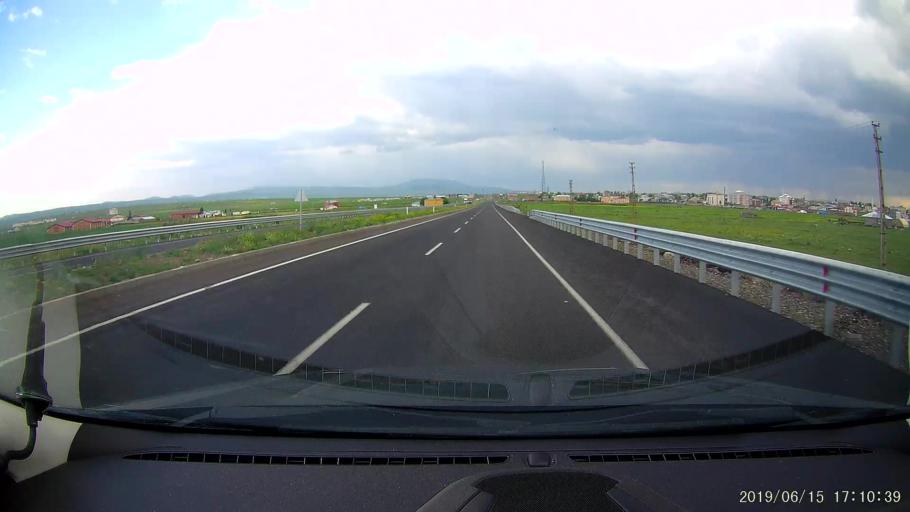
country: TR
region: Kars
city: Kars
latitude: 40.6199
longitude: 43.1336
